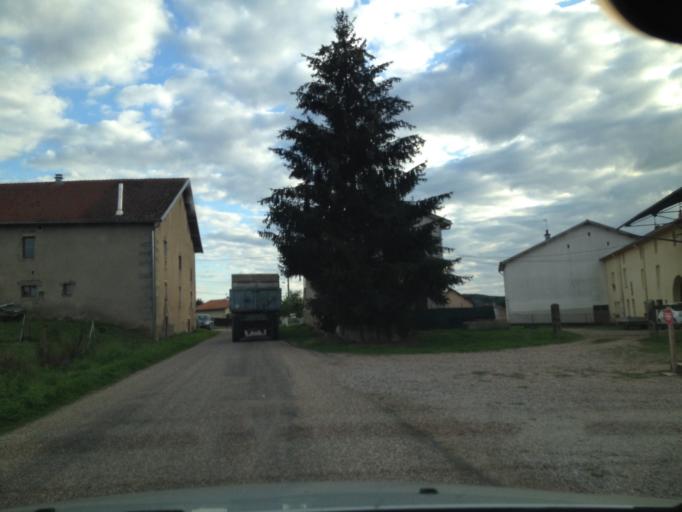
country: FR
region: Lorraine
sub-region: Departement des Vosges
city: Bains-les-Bains
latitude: 47.9828
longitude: 6.2071
